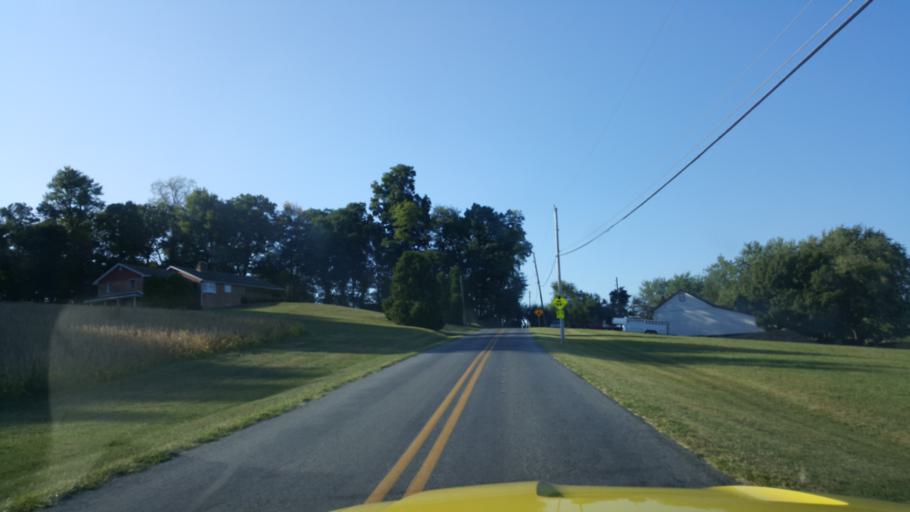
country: US
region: Pennsylvania
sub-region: Lancaster County
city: Rheems
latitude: 40.1730
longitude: -76.5476
